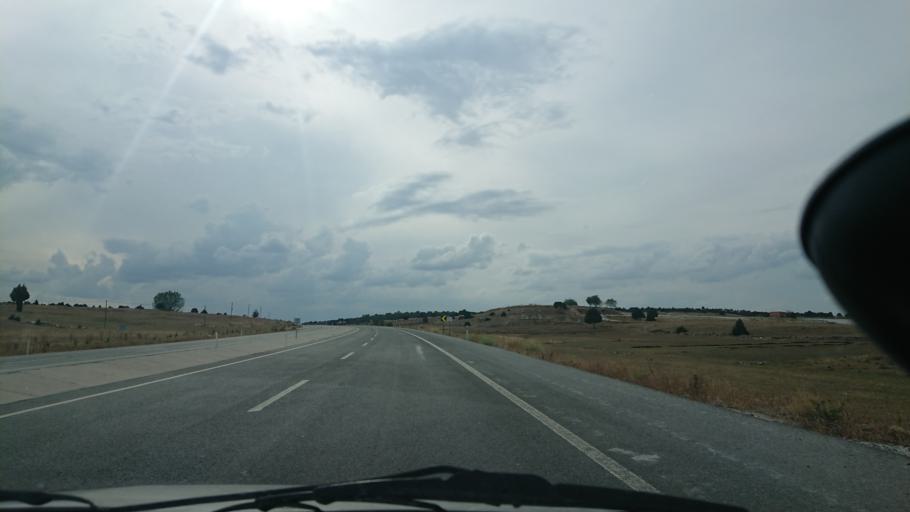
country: TR
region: Kuetahya
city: Aslanapa
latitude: 39.2331
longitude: 29.7767
